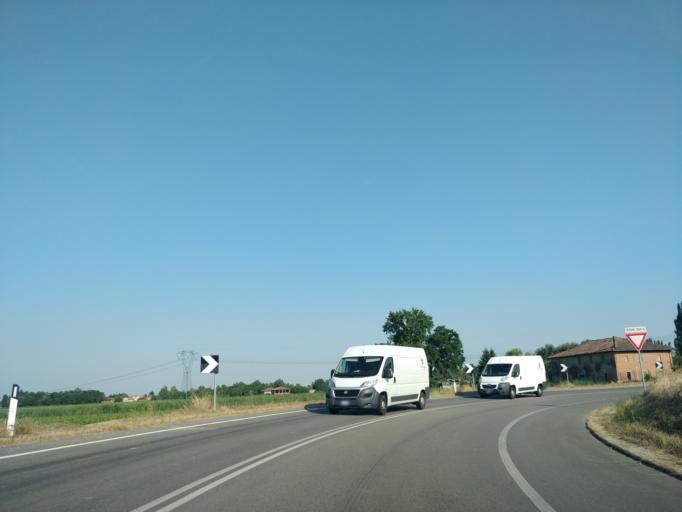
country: IT
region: Emilia-Romagna
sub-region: Provincia di Bologna
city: Castel Maggiore
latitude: 44.6010
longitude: 11.3481
